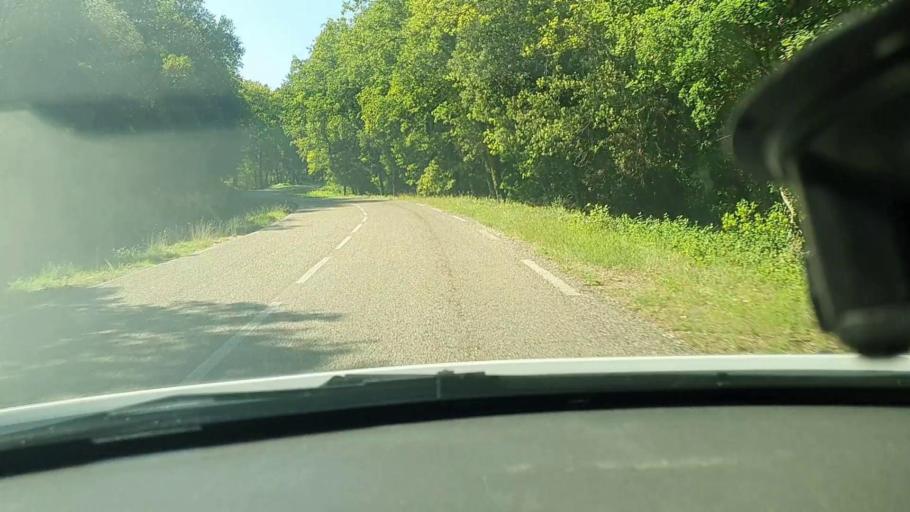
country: FR
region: Languedoc-Roussillon
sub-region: Departement du Gard
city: Saint-Paulet-de-Caisson
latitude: 44.2370
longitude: 4.5680
